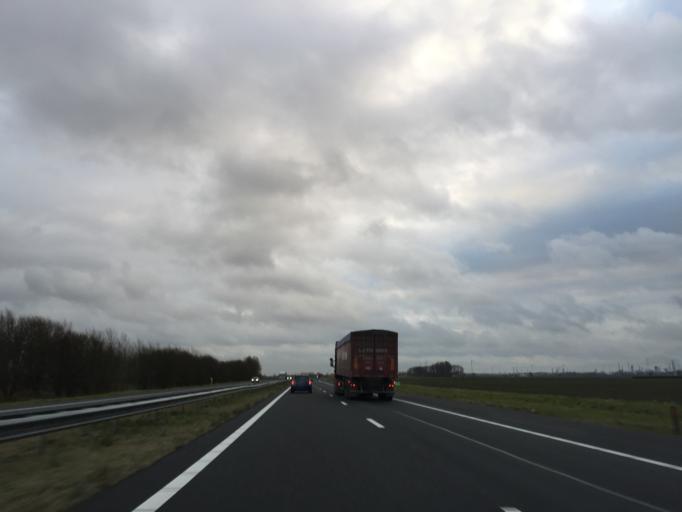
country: NL
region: North Brabant
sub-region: Gemeente Woensdrecht
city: Woensdrecht
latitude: 51.4100
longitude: 4.2820
